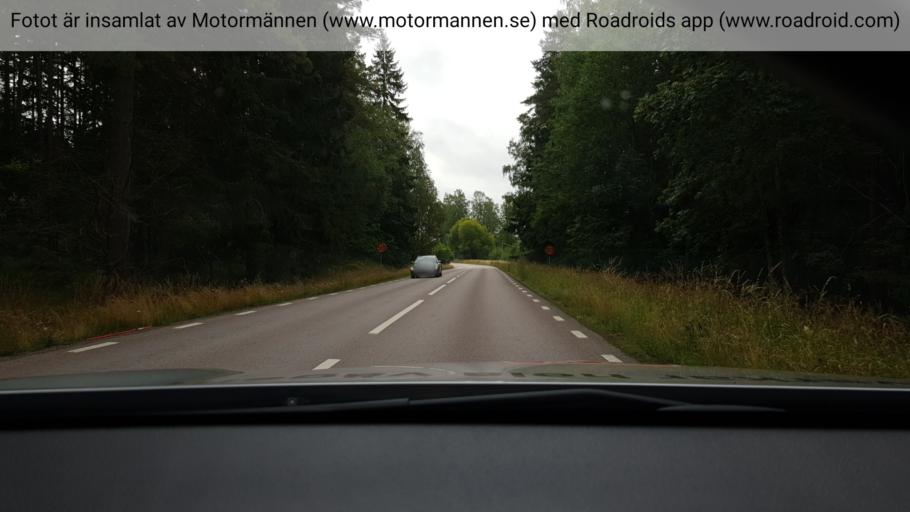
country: SE
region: Soedermanland
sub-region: Strangnas Kommun
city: Mariefred
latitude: 59.2108
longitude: 17.1827
